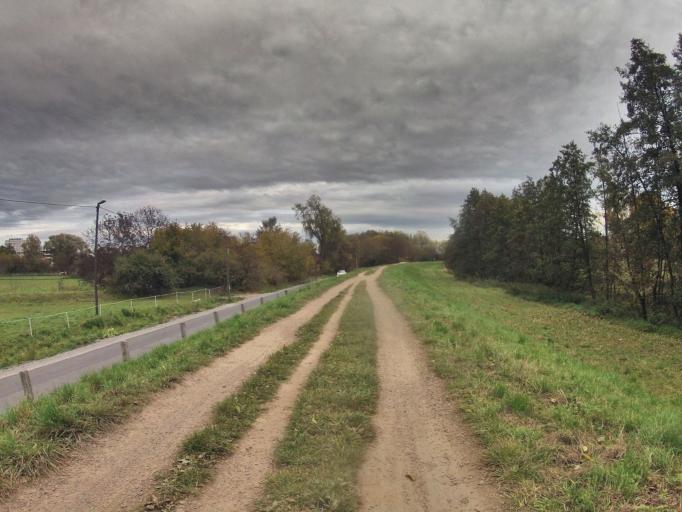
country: PL
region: Lesser Poland Voivodeship
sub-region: Krakow
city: Krakow
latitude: 50.0670
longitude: 19.8893
